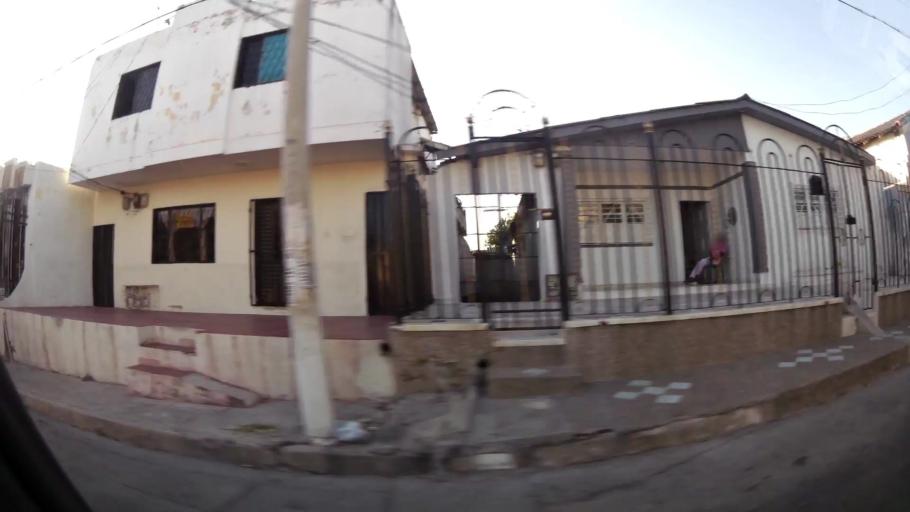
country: CO
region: Atlantico
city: Barranquilla
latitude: 10.9777
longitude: -74.7921
